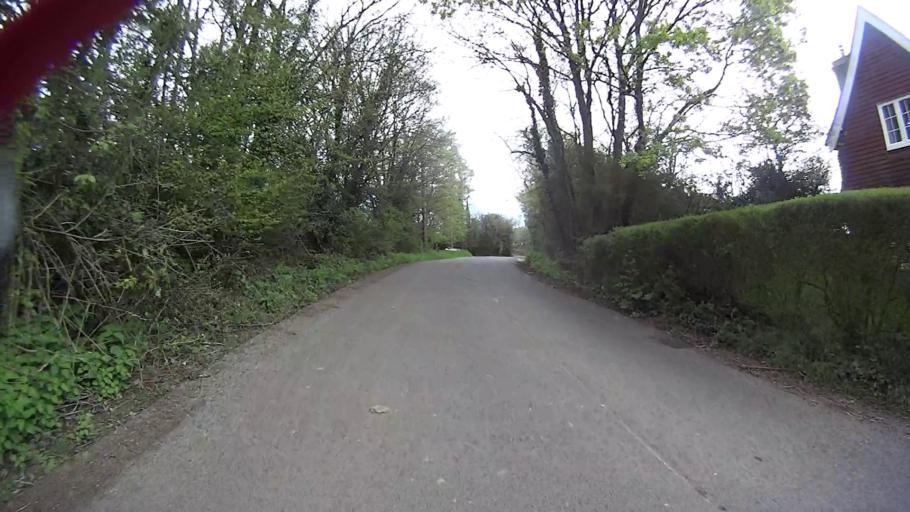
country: GB
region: England
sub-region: Surrey
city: Newdigate
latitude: 51.1341
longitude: -0.2628
